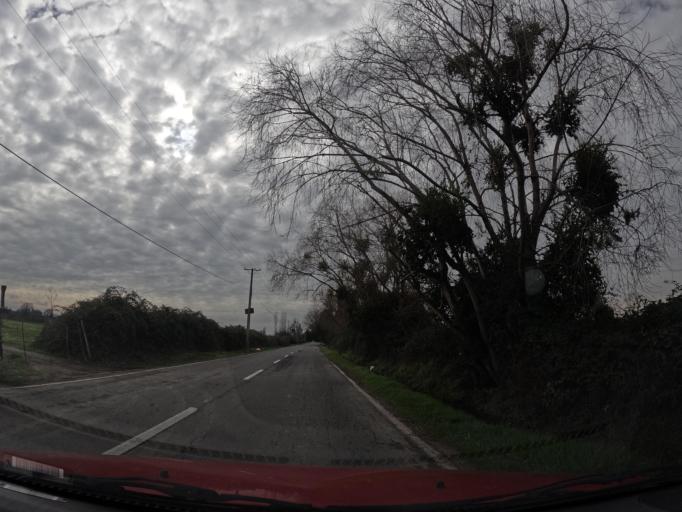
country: CL
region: Maule
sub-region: Provincia de Linares
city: Linares
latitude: -35.8616
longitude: -71.6170
